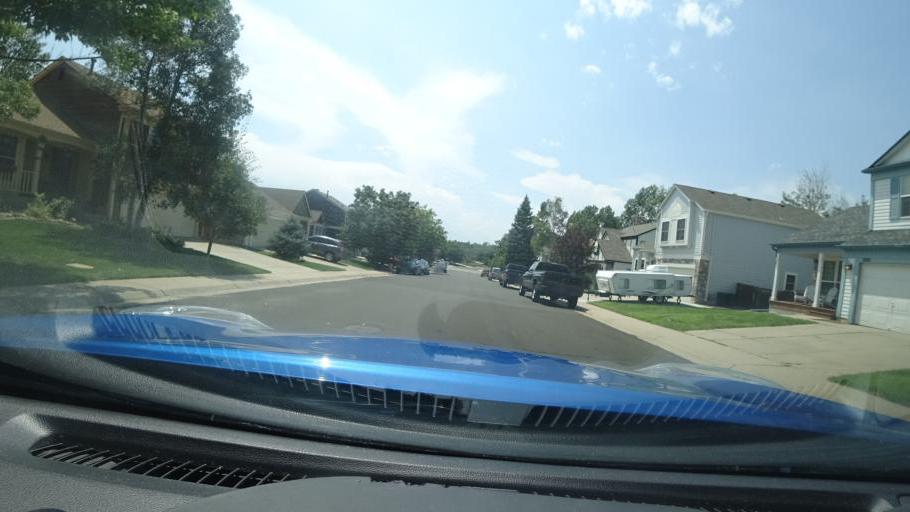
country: US
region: Colorado
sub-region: Adams County
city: Aurora
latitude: 39.6656
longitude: -104.7619
